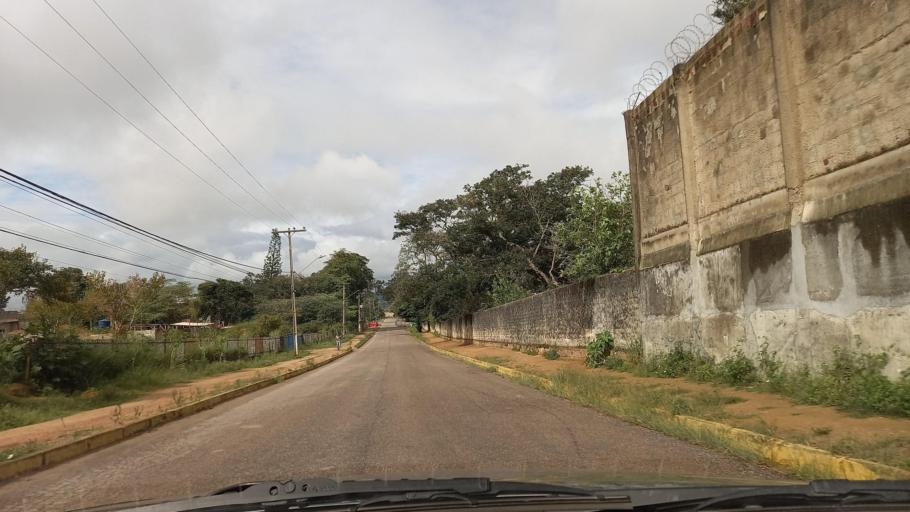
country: BR
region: Pernambuco
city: Garanhuns
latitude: -8.9035
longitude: -36.4945
